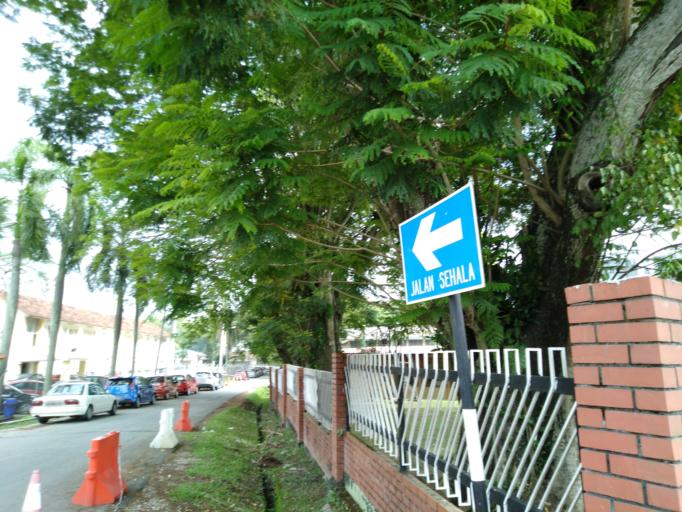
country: MY
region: Perak
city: Ipoh
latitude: 4.6011
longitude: 101.0892
